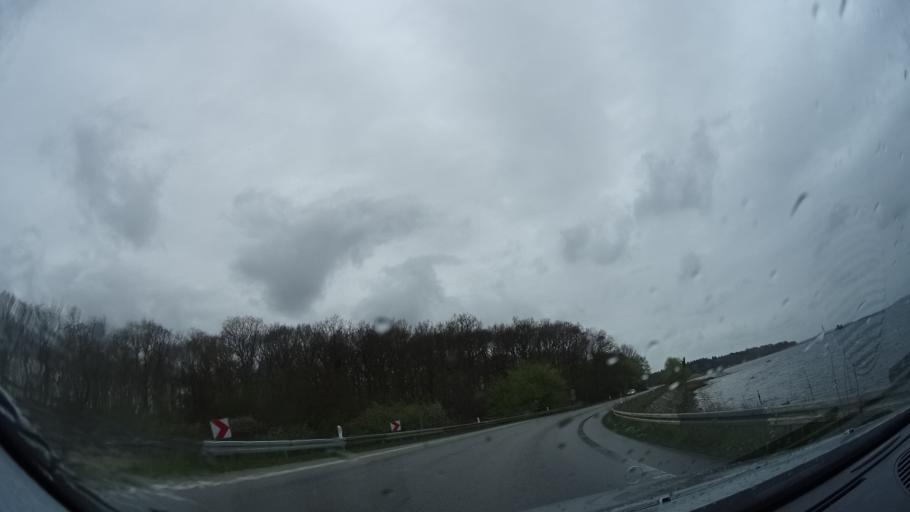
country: DK
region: Zealand
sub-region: Lejre Kommune
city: Ejby
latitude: 55.6739
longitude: 11.8076
